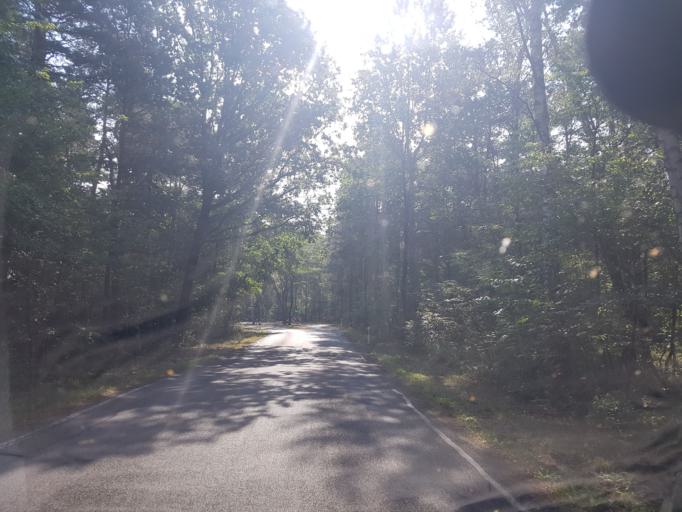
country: DE
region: Brandenburg
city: Lauchhammer
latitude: 51.5102
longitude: 13.7321
